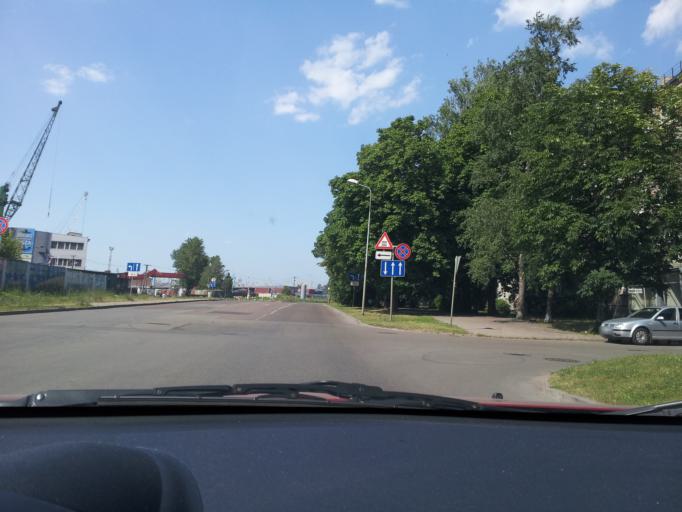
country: LV
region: Riga
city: Riga
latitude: 56.9699
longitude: 24.0978
